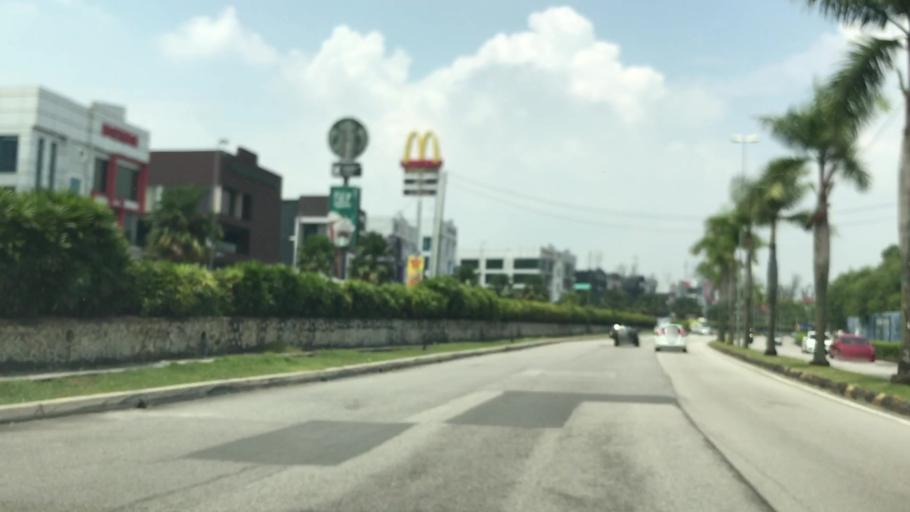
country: MY
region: Selangor
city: Subang Jaya
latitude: 3.0210
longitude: 101.6243
